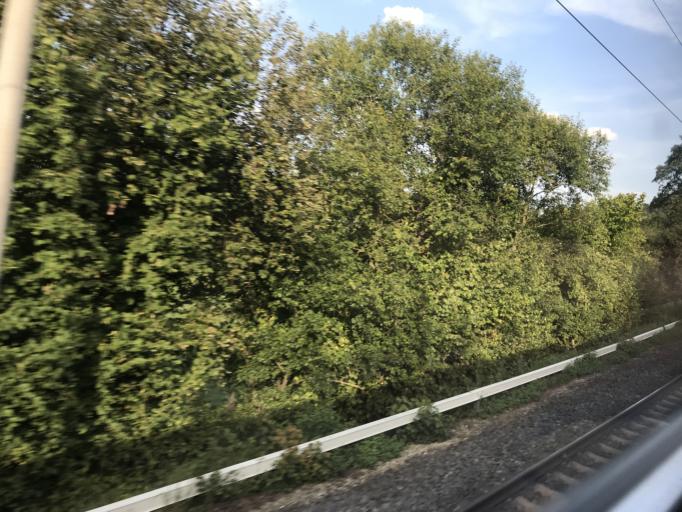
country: DE
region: Hesse
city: Bad Camberg
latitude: 50.3344
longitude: 8.2215
